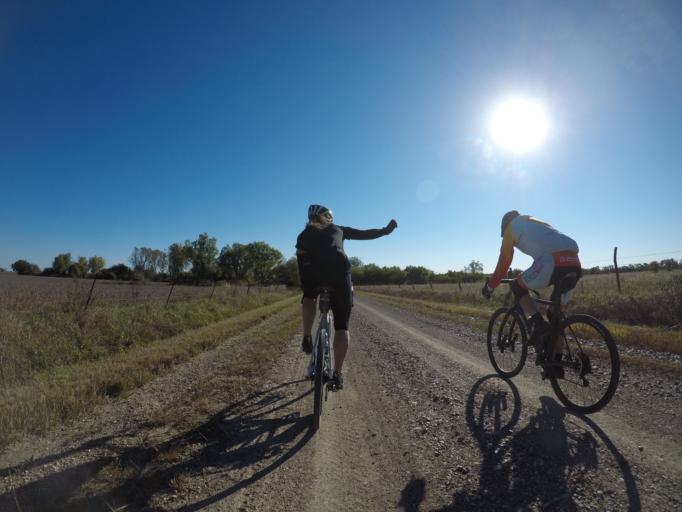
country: US
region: Kansas
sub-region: Morris County
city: Council Grove
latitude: 38.8256
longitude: -96.4323
